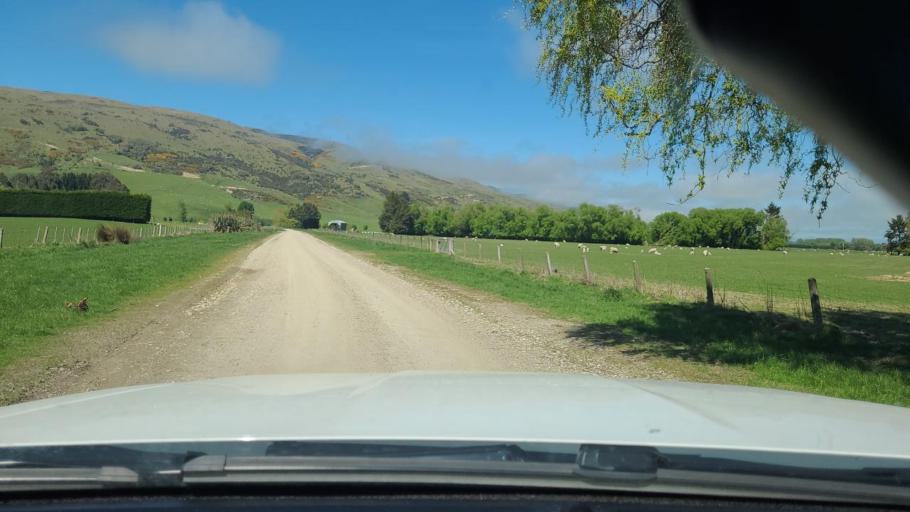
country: NZ
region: Southland
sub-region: Gore District
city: Gore
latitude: -45.7298
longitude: 168.8441
